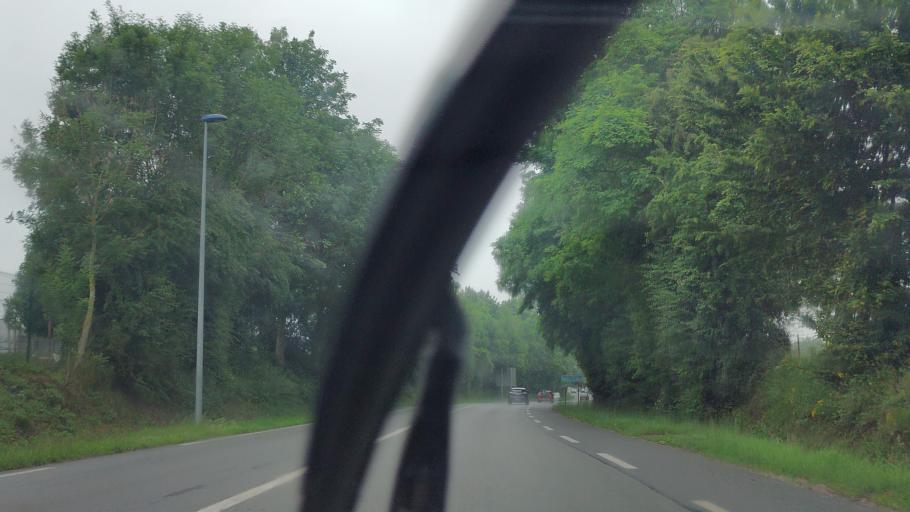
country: FR
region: Picardie
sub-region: Departement de la Somme
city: Fressenneville
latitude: 50.0735
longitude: 1.5882
